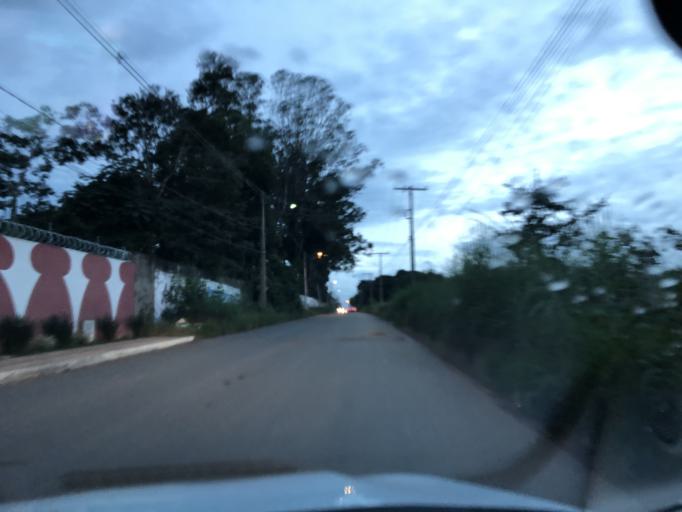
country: BR
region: Goias
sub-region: Luziania
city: Luziania
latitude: -16.1114
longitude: -47.9894
